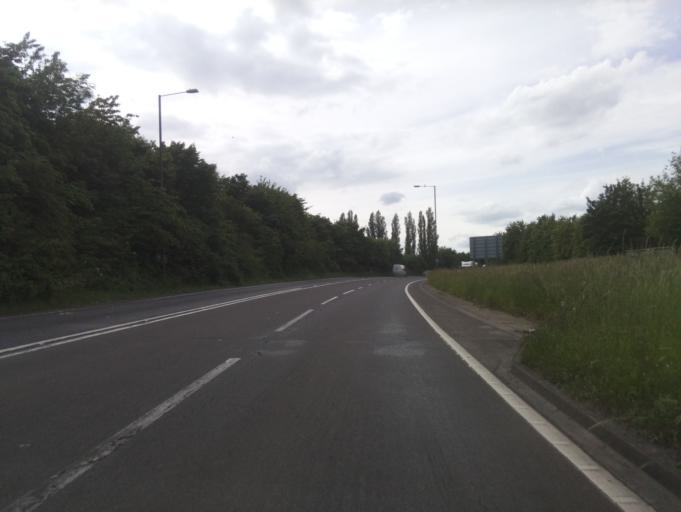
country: GB
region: England
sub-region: Worcestershire
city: Worcester
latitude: 52.1814
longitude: -2.2588
